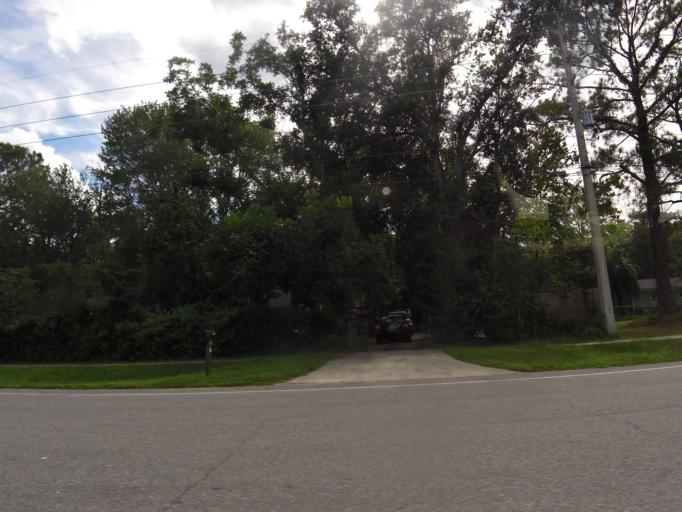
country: US
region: Florida
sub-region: Clay County
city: Lakeside
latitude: 30.1291
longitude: -81.7721
